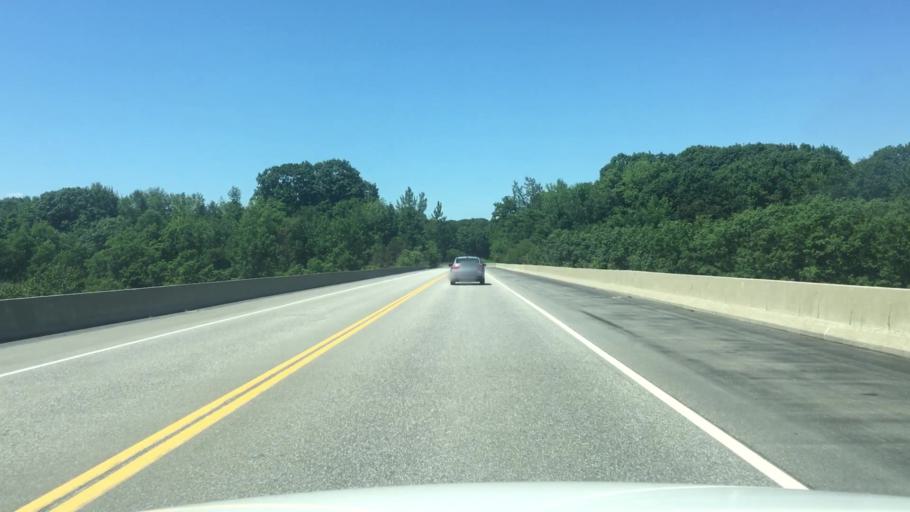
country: US
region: Maine
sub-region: Kennebec County
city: Waterville
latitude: 44.5311
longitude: -69.6468
